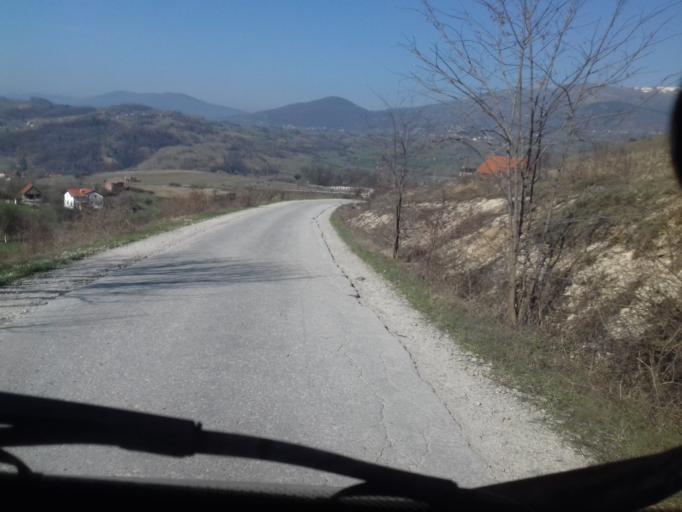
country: BA
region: Federation of Bosnia and Herzegovina
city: Vitez
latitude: 44.2402
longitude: 17.7726
